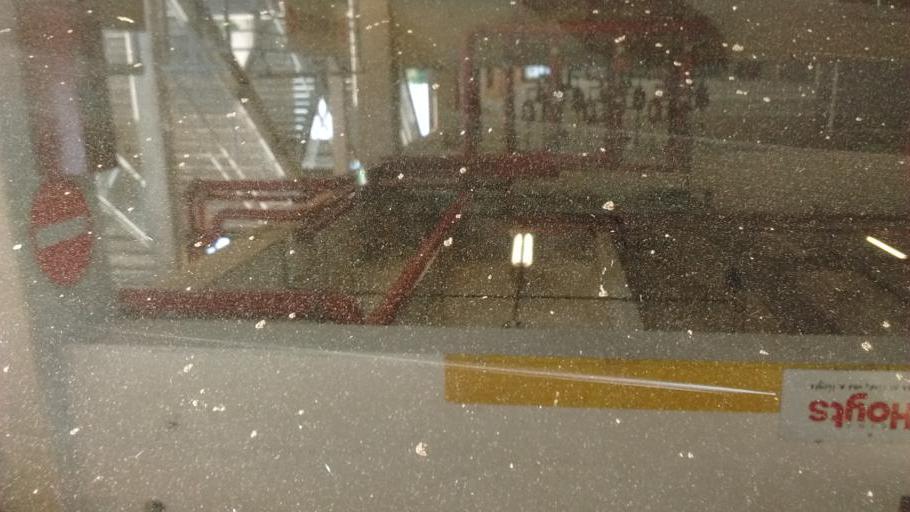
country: AR
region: Santa Fe
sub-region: Departamento de Rosario
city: Rosario
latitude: -32.9108
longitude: -60.6841
